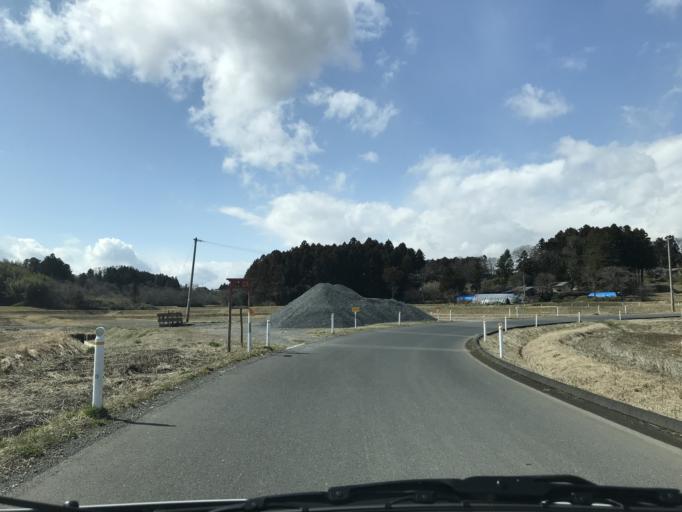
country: JP
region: Miyagi
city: Wakuya
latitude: 38.6758
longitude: 141.1200
